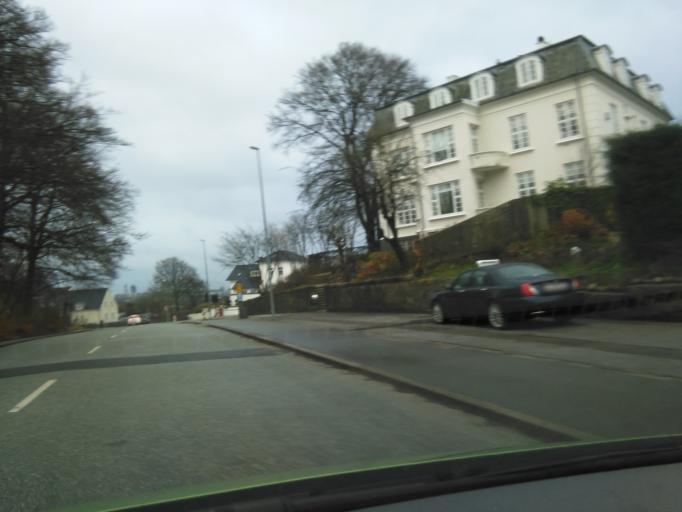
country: DK
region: Central Jutland
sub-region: Arhus Kommune
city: Arhus
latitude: 56.1333
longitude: 10.2072
